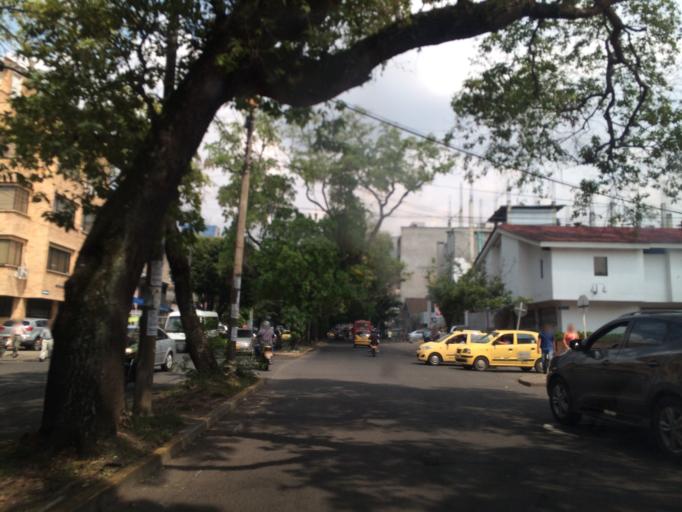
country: CO
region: Valle del Cauca
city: Cali
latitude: 3.4213
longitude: -76.5454
